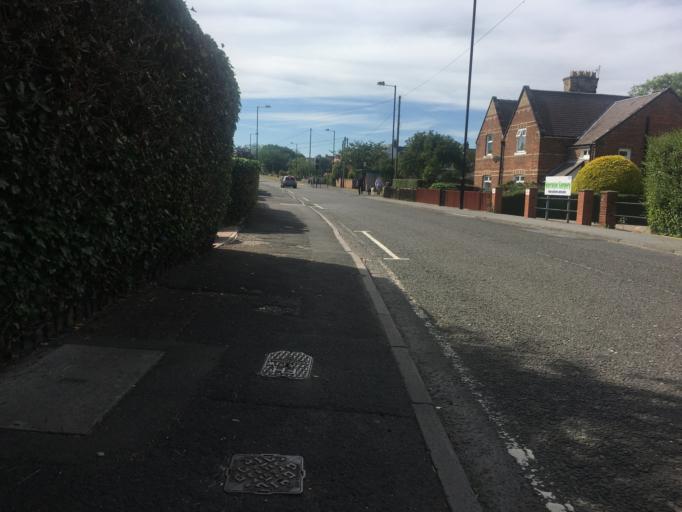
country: GB
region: England
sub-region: Sunderland
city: Washington
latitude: 54.8808
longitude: -1.5311
